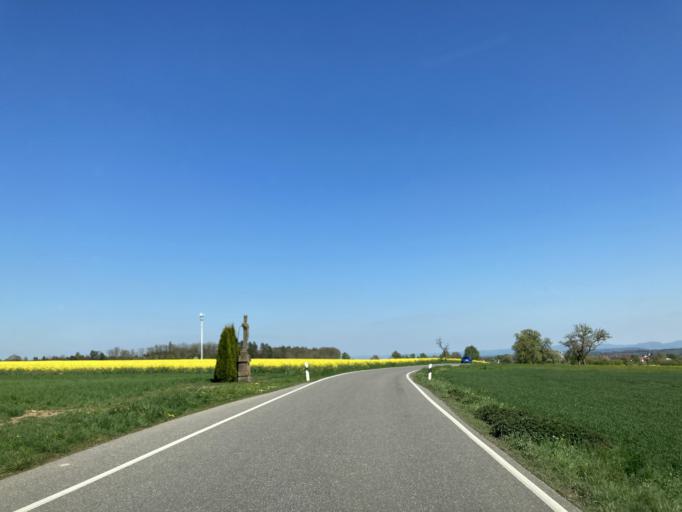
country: DE
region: Baden-Wuerttemberg
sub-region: Regierungsbezirk Stuttgart
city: Motzingen
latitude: 48.5118
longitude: 8.7575
